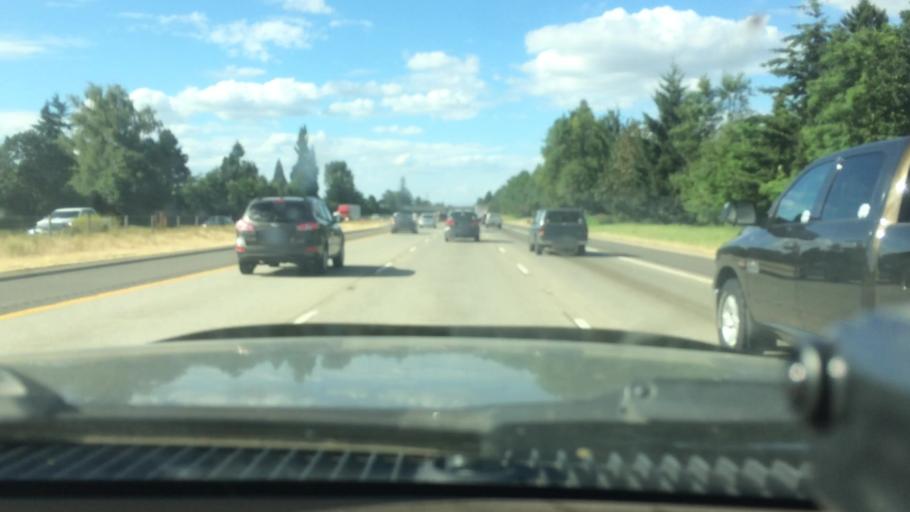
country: US
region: Oregon
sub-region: Marion County
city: Four Corners
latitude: 44.9341
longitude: -122.9912
